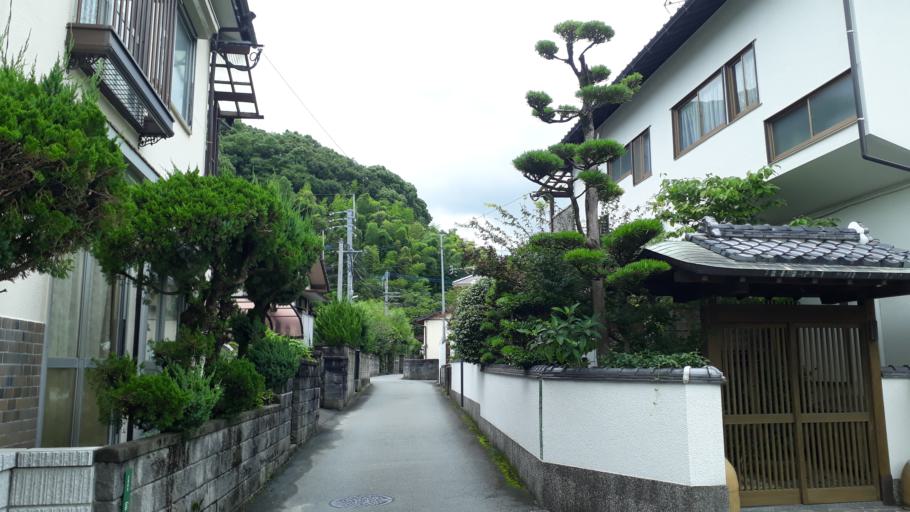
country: JP
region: Fukuoka
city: Dazaifu
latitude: 33.5192
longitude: 130.5350
